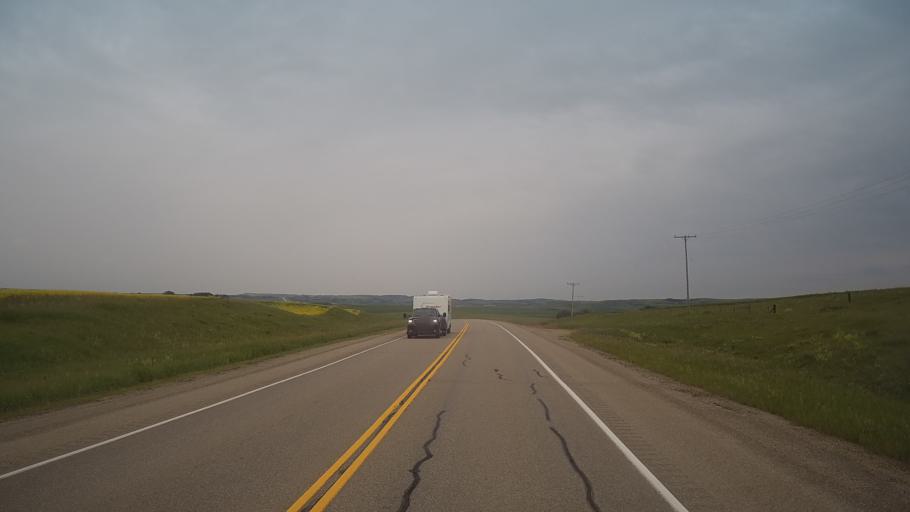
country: CA
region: Saskatchewan
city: Biggar
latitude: 52.0557
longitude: -107.7757
